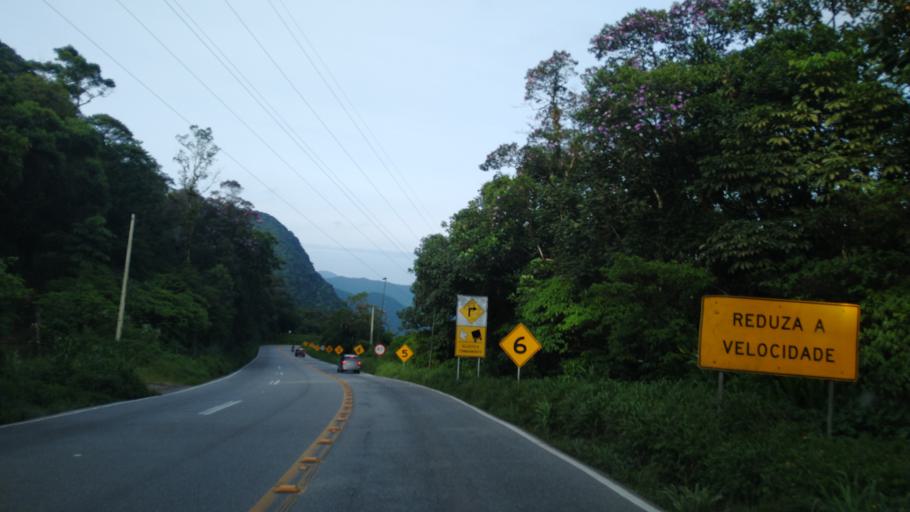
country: BR
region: Santa Catarina
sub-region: Schroeder
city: Schroeder
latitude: -26.1954
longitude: -49.0398
